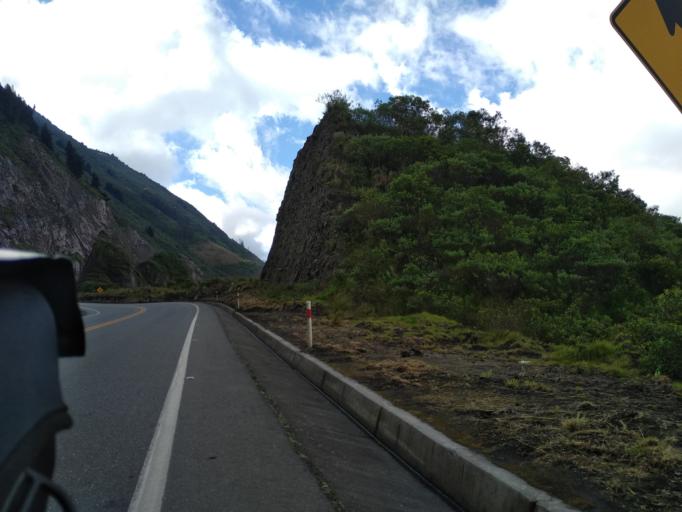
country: EC
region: Tungurahua
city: Banos
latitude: -1.4861
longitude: -78.5179
